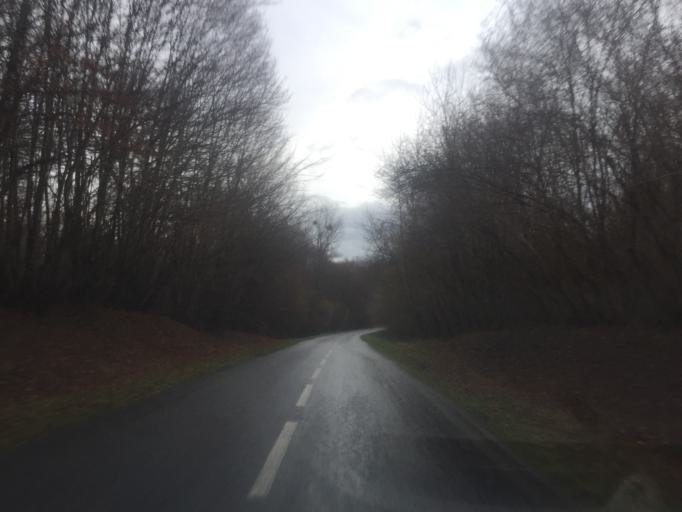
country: FR
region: Bourgogne
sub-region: Departement de la Cote-d'Or
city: Auxonne
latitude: 47.2298
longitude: 5.4715
